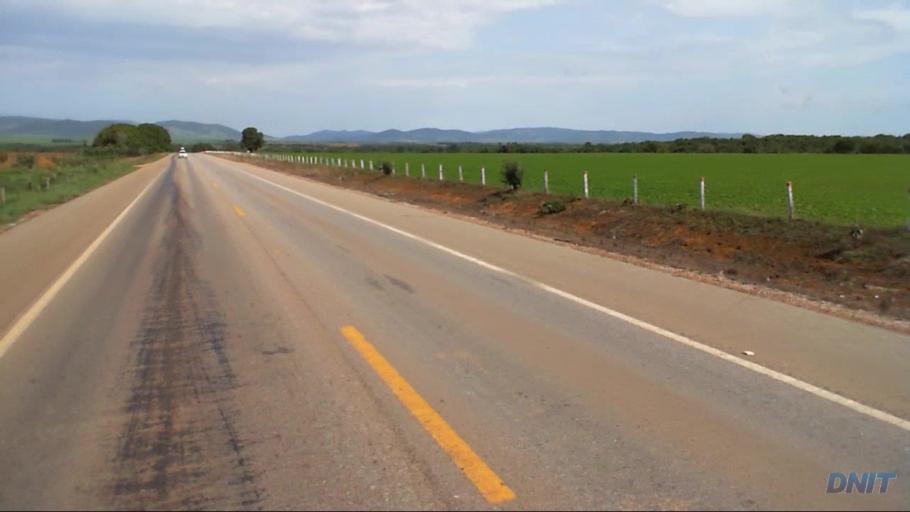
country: BR
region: Goias
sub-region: Barro Alto
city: Barro Alto
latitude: -15.1064
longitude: -48.8466
